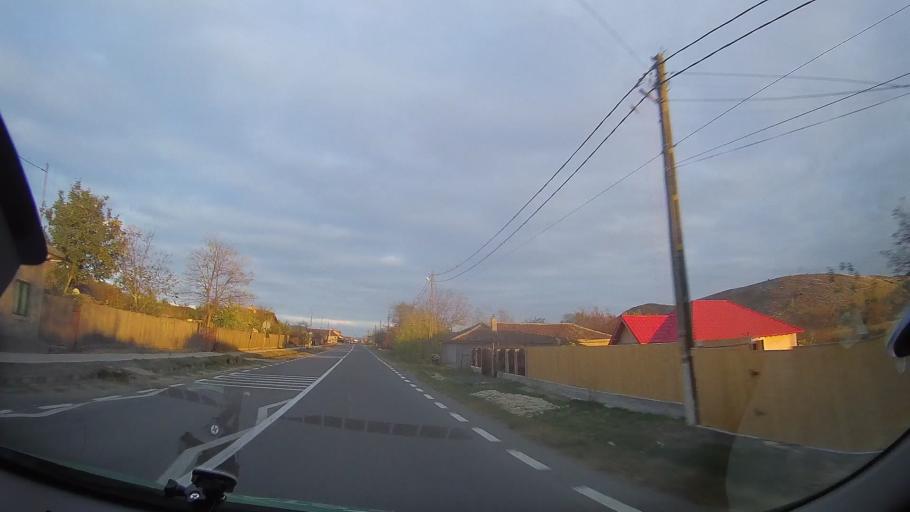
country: RO
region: Tulcea
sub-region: Comuna Nalbant
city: Nicolae Balcescu
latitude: 44.9946
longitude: 28.5841
